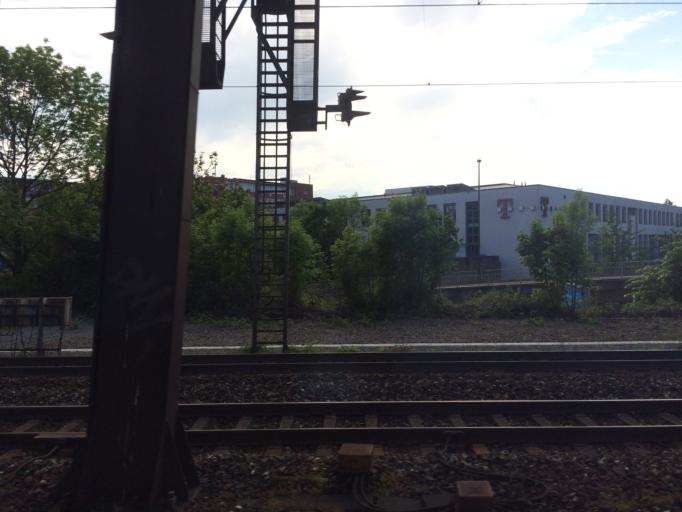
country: DE
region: Bavaria
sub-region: Regierungsbezirk Unterfranken
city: Wuerzburg
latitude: 49.7990
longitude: 9.9506
